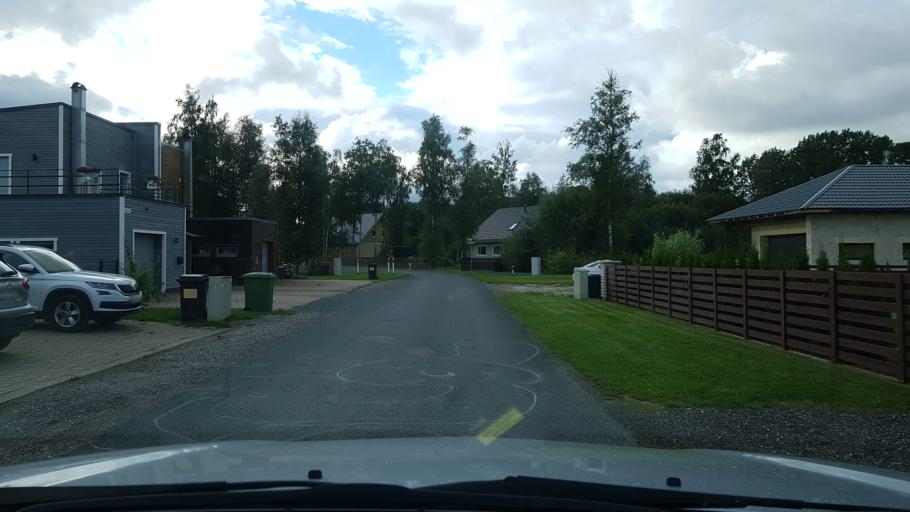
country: EE
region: Harju
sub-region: Rae vald
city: Jueri
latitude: 59.3665
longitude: 24.9183
